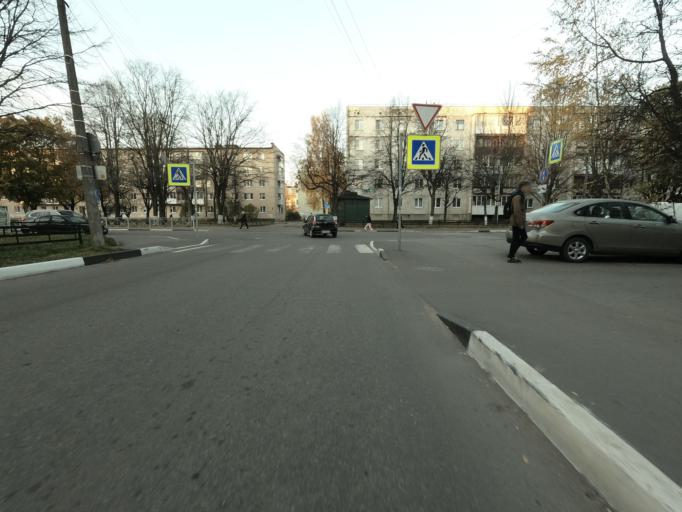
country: RU
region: Leningrad
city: Kirovsk
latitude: 59.8806
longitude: 30.9908
